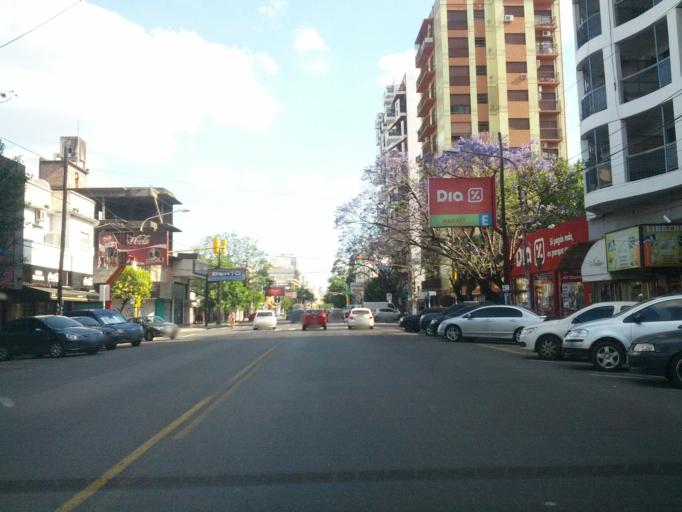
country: AR
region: Buenos Aires
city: San Justo
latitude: -34.6476
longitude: -58.5642
